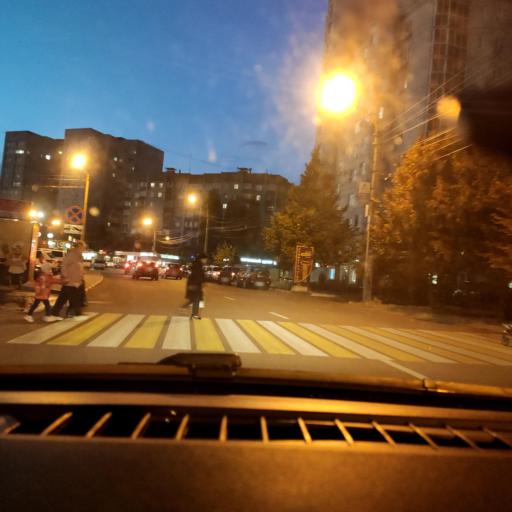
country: RU
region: Voronezj
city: Podgornoye
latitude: 51.7172
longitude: 39.1749
